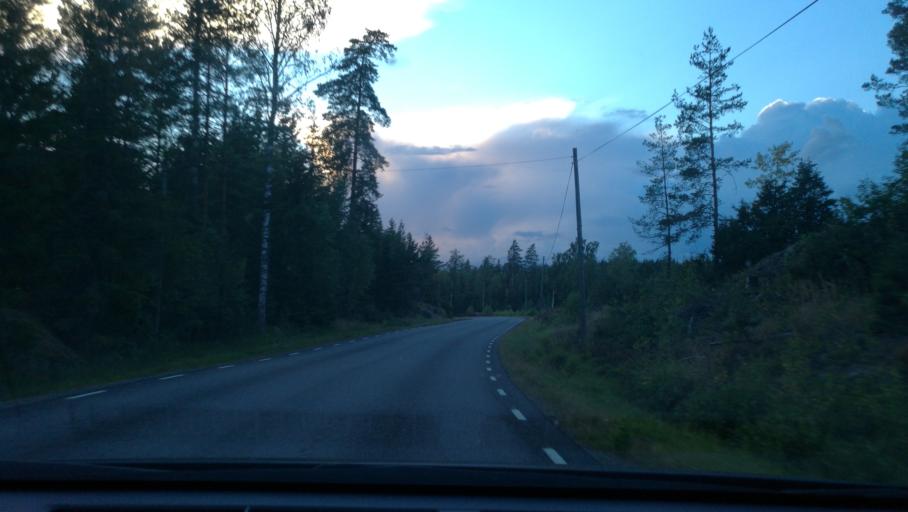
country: SE
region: OEstergoetland
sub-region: Norrkopings Kommun
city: Jursla
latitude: 58.8041
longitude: 16.1279
